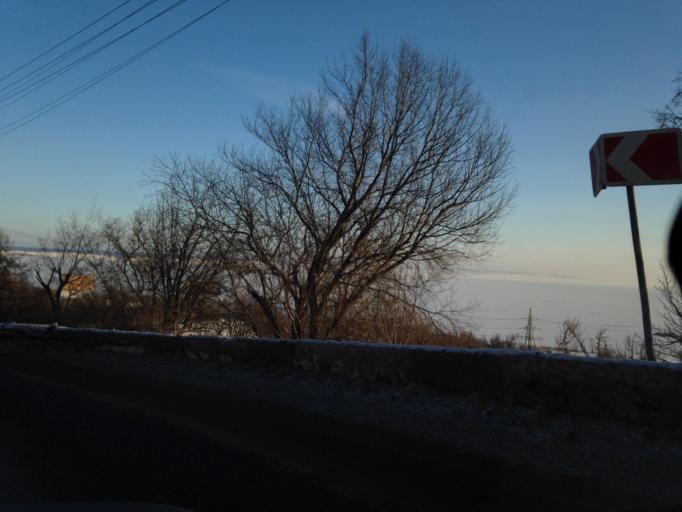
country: RU
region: Ulyanovsk
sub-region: Ulyanovskiy Rayon
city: Ulyanovsk
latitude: 54.3046
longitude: 48.3938
